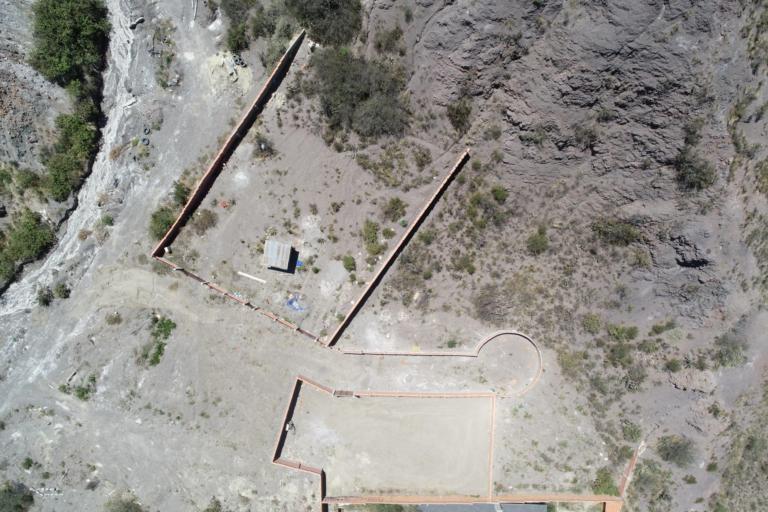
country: BO
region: La Paz
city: La Paz
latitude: -16.6188
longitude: -68.0566
